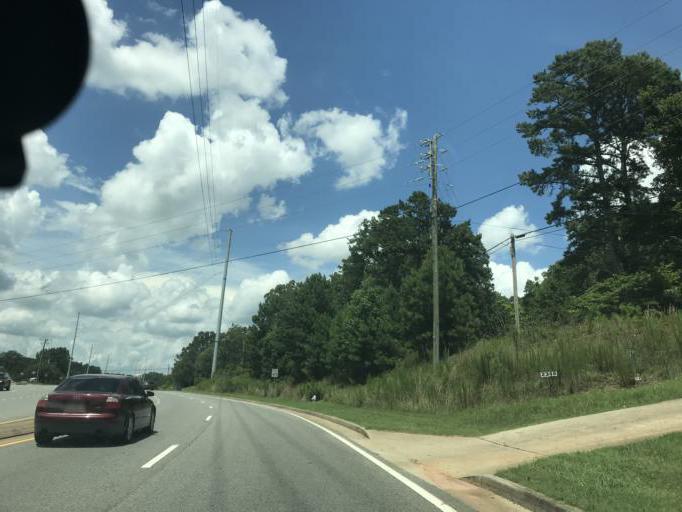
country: US
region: Georgia
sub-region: Forsyth County
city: Cumming
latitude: 34.1562
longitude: -84.1541
